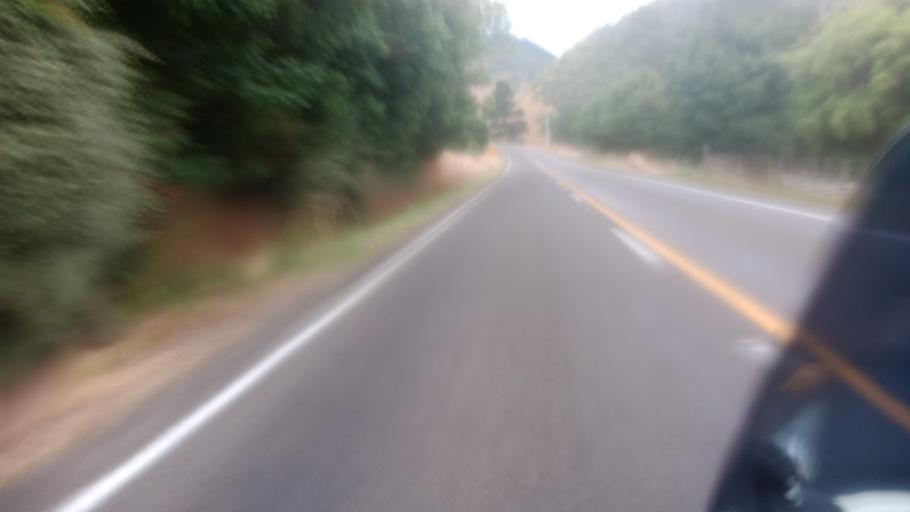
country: NZ
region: Bay of Plenty
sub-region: Opotiki District
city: Opotiki
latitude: -38.3674
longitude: 177.4876
